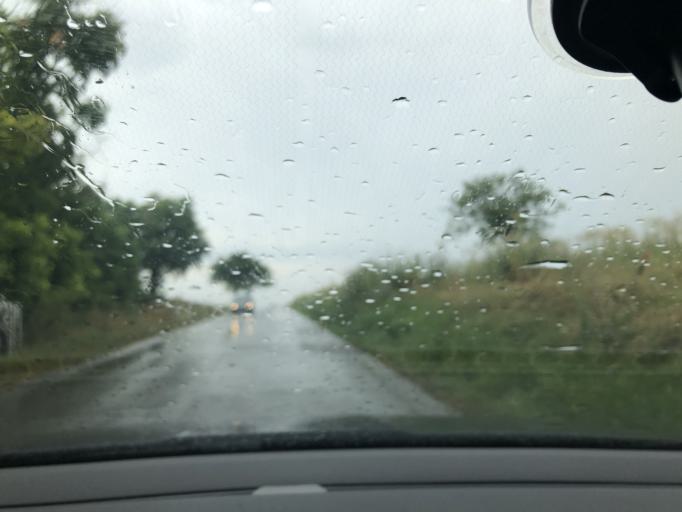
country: AT
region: Lower Austria
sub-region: Politischer Bezirk Ganserndorf
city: Auersthal
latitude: 48.3754
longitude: 16.6435
